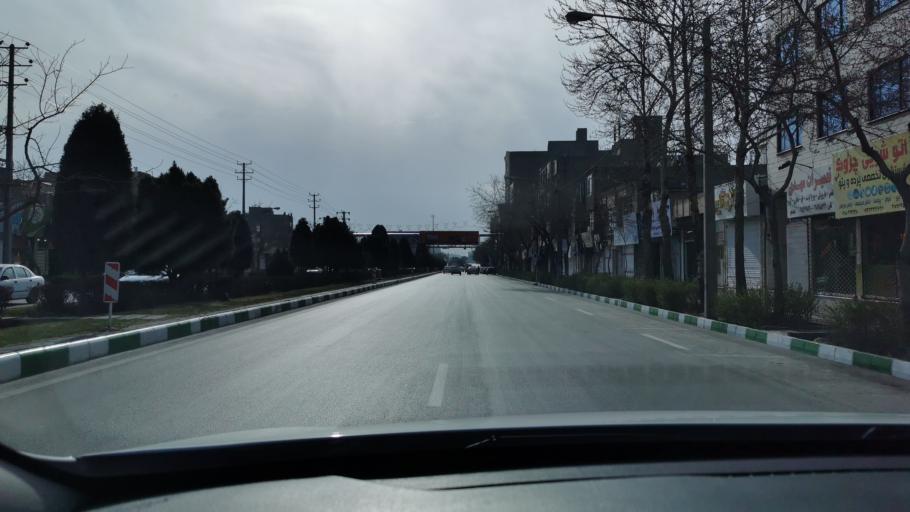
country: IR
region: Razavi Khorasan
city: Mashhad
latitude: 36.2977
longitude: 59.5264
